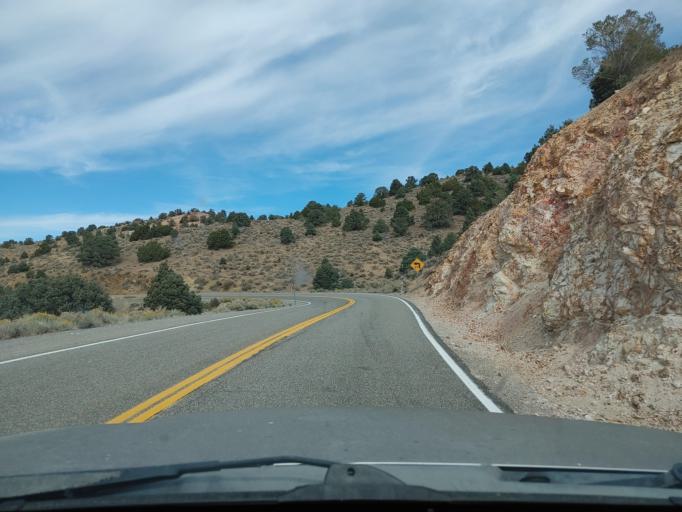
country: US
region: Nevada
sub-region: Storey County
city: Virginia City
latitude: 39.2946
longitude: -119.6437
